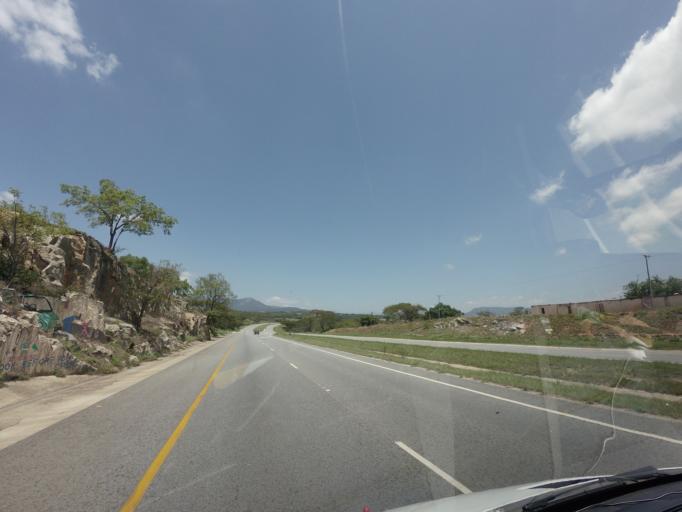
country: ZA
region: Mpumalanga
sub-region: Ehlanzeni District
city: Nelspruit
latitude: -25.4459
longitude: 30.8702
